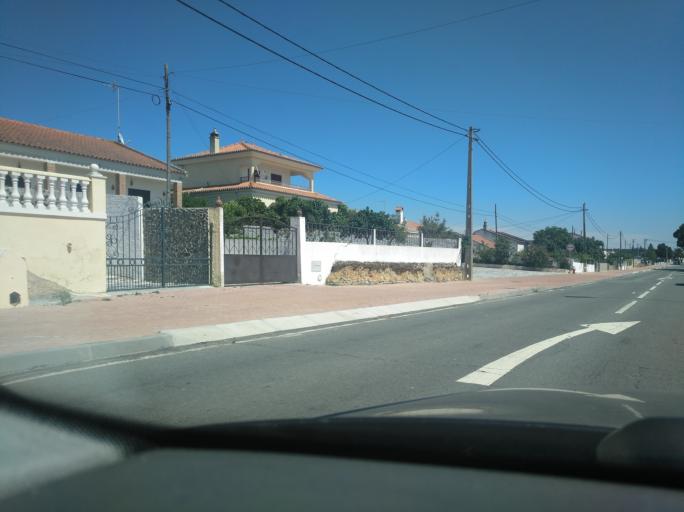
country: PT
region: Beja
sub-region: Castro Verde
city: Castro Verde
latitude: 37.6114
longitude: -8.0821
